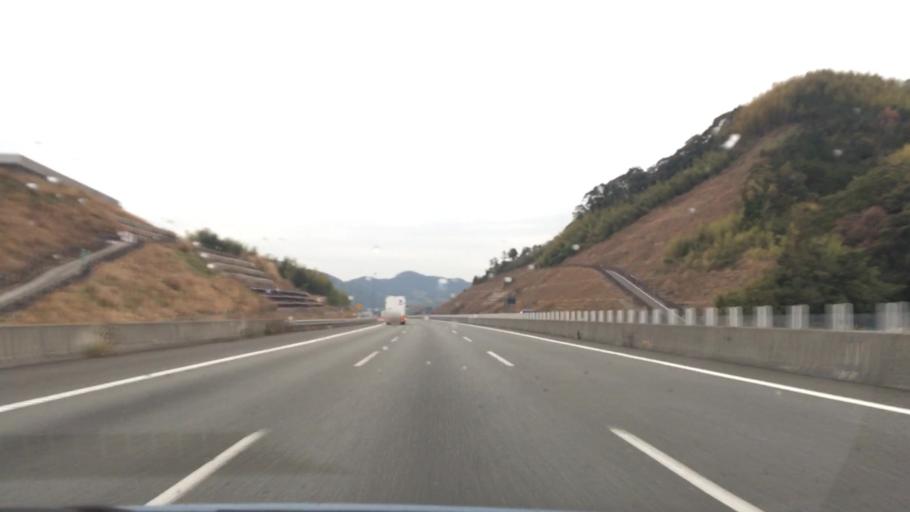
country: JP
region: Shizuoka
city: Fujieda
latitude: 34.9137
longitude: 138.2585
